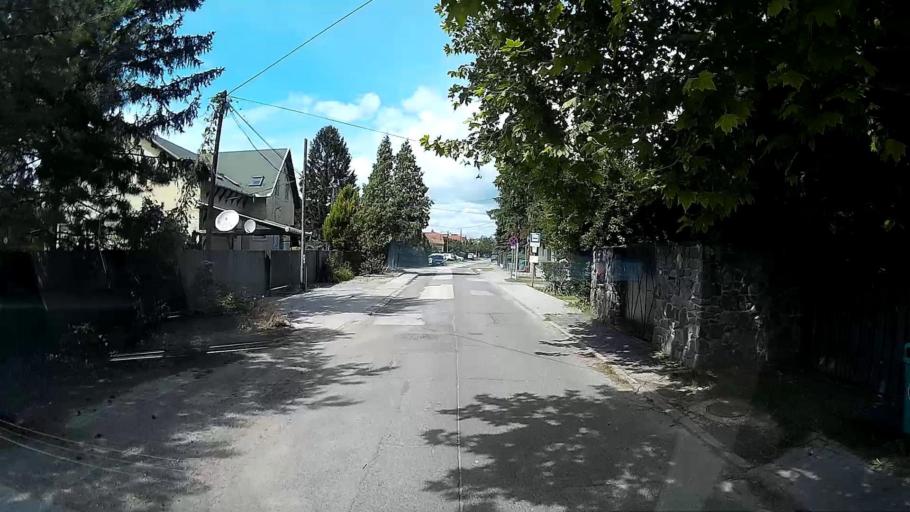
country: HU
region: Pest
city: Leanyfalu
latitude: 47.7181
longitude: 19.0978
